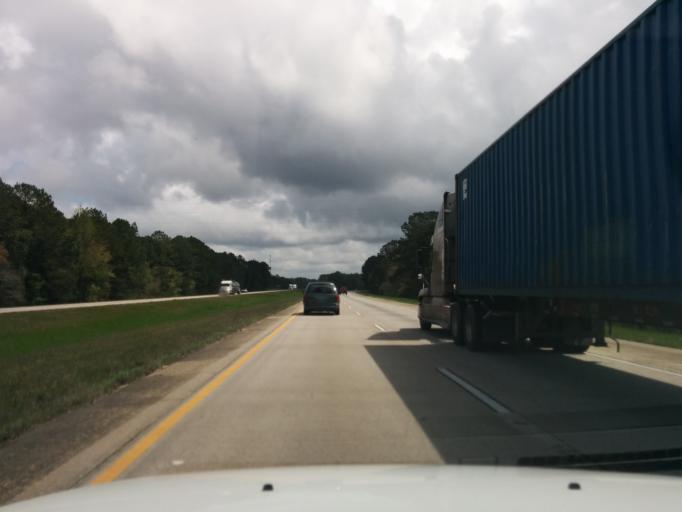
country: US
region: Georgia
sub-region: Evans County
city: Claxton
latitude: 32.3033
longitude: -81.8483
